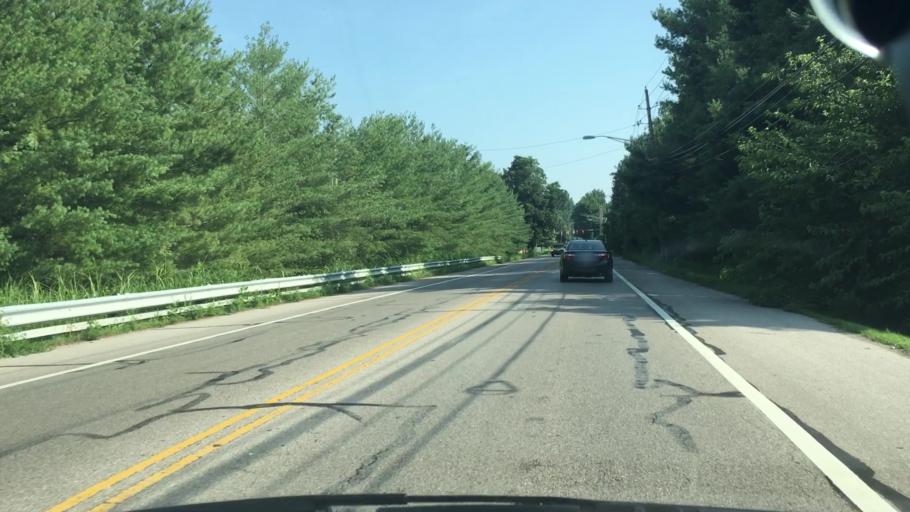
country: US
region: Indiana
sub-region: Vanderburgh County
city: Melody Hill
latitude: 37.9726
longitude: -87.4743
